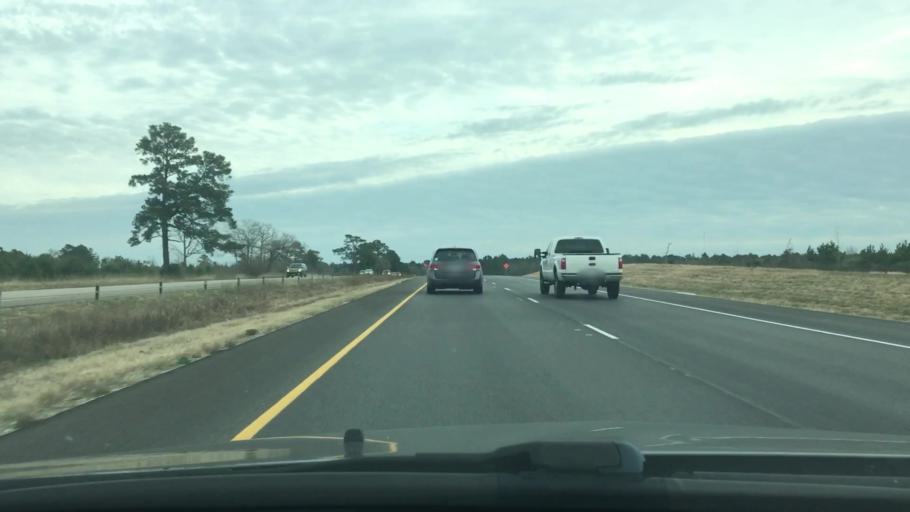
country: US
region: Texas
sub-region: Madison County
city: Madisonville
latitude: 30.8444
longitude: -95.7289
